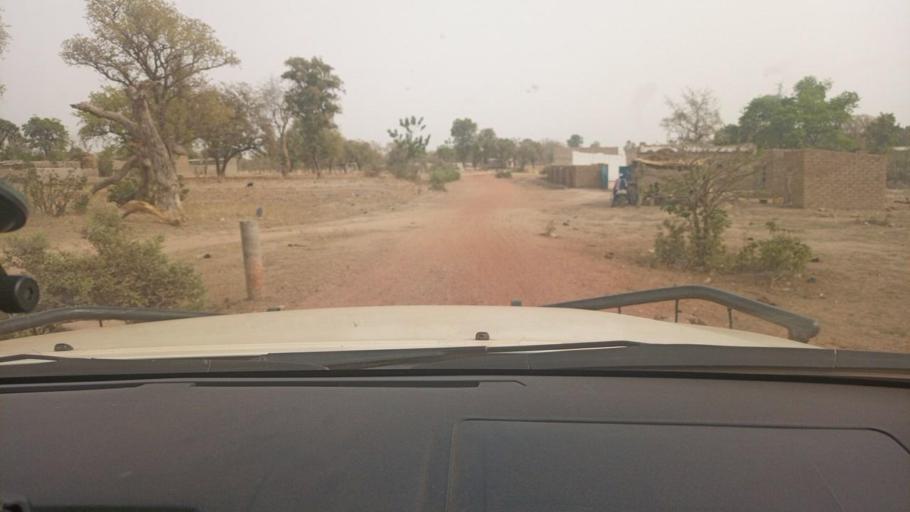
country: BF
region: Boucle du Mouhoun
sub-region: Province des Banwa
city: Salanso
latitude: 12.1130
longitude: -4.3376
